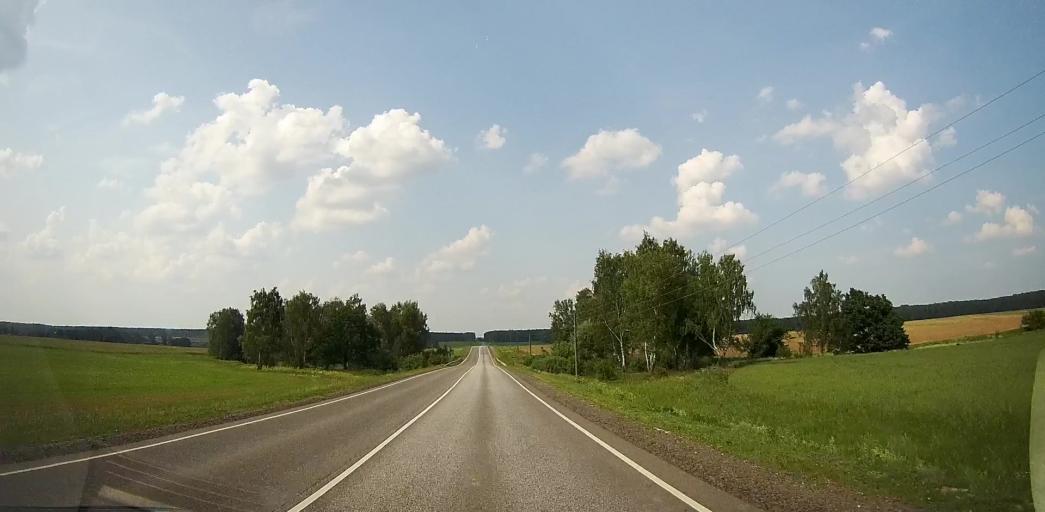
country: RU
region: Moskovskaya
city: Malino
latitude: 55.0407
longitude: 38.1530
